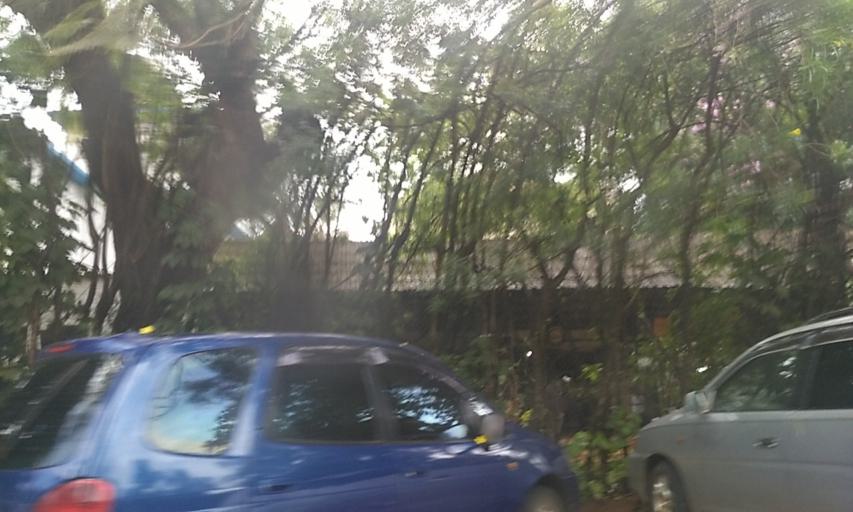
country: UG
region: Central Region
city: Kampala Central Division
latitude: 0.3331
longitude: 32.5862
